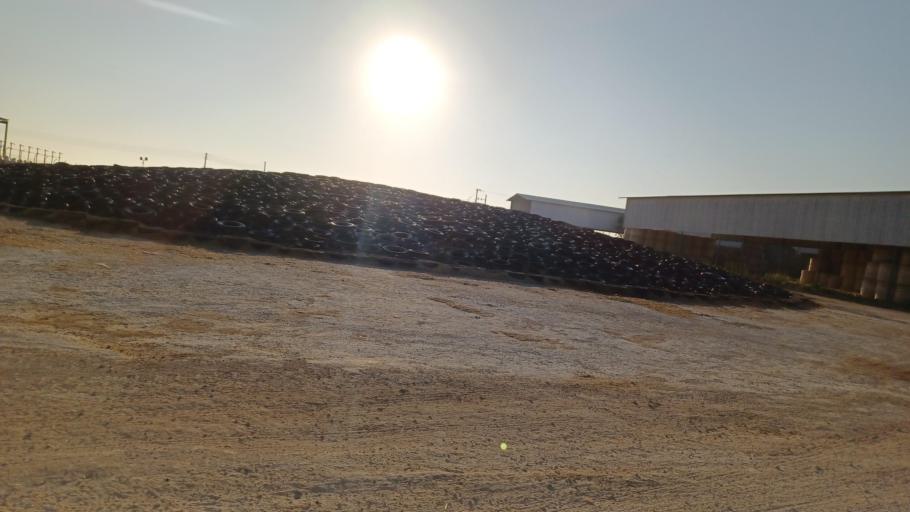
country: CY
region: Ammochostos
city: Avgorou
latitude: 35.0153
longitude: 33.8017
